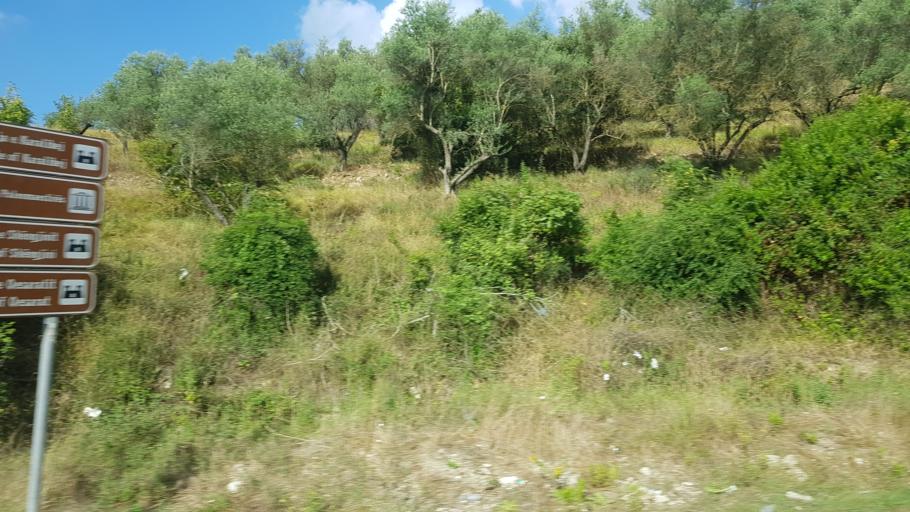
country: AL
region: Vlore
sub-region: Rrethi i Delvines
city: Mesopotam
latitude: 39.9025
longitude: 20.0852
